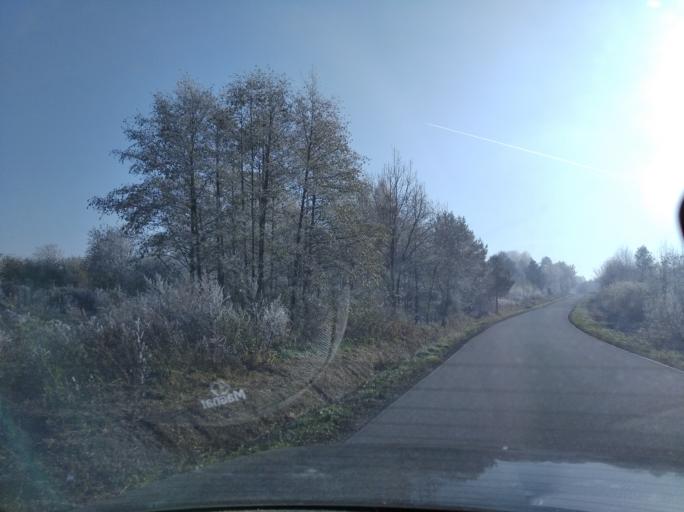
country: PL
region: Subcarpathian Voivodeship
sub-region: Powiat strzyzowski
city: Wysoka Strzyzowska
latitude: 49.8444
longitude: 21.7042
